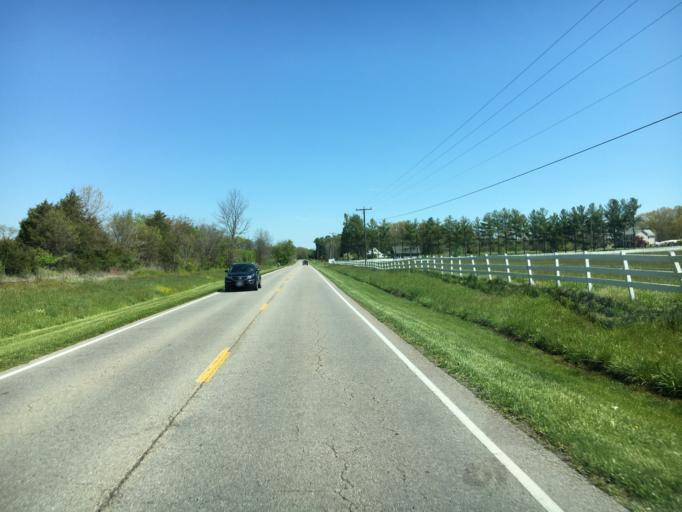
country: US
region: Virginia
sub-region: Rockingham County
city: Grottoes
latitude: 38.2347
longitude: -78.8300
